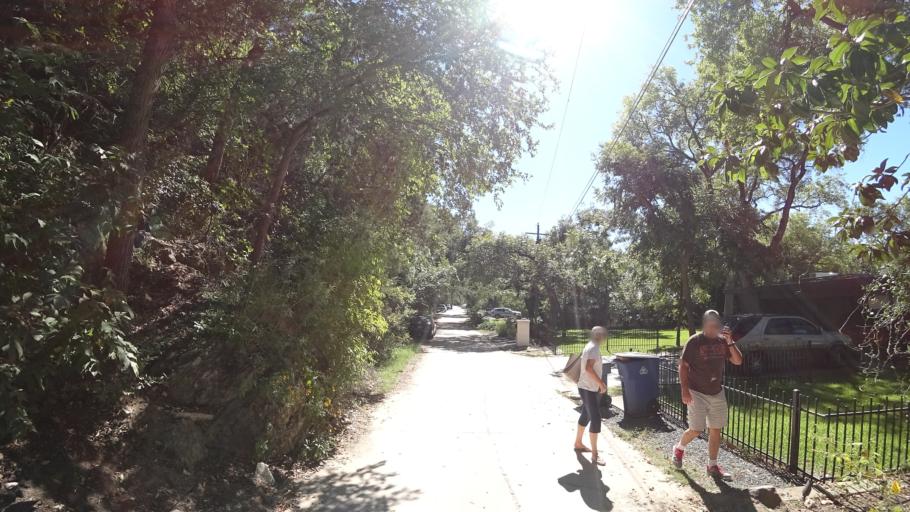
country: US
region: Texas
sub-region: Travis County
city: West Lake Hills
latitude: 30.3371
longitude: -97.7822
